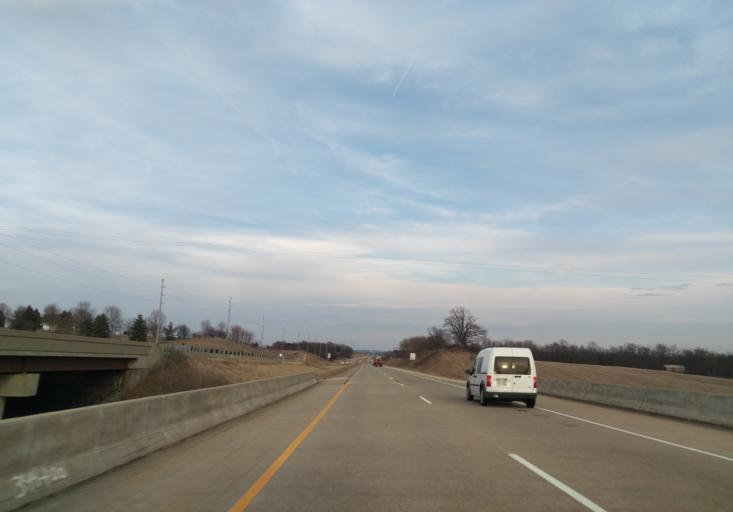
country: US
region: Wisconsin
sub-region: Dane County
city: Verona
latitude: 42.9881
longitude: -89.6271
